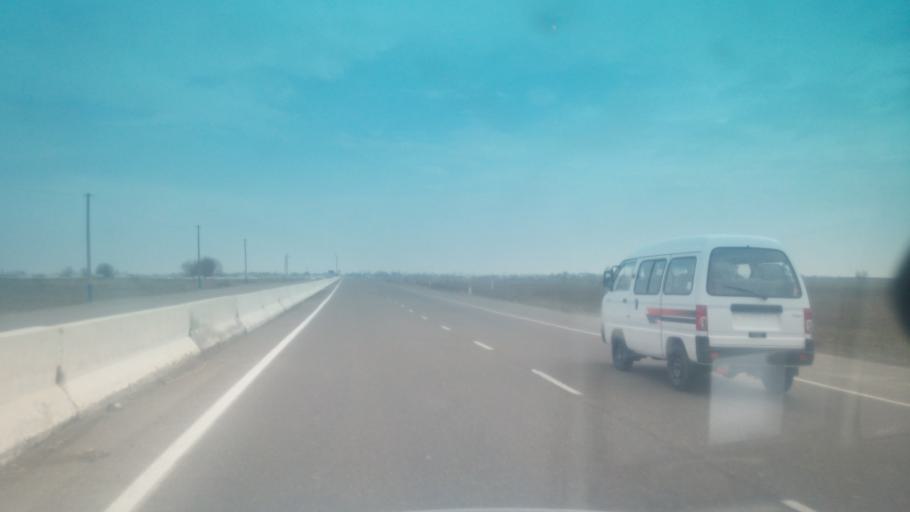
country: KZ
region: Ongtustik Qazaqstan
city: Myrzakent
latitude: 40.5016
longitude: 68.5428
